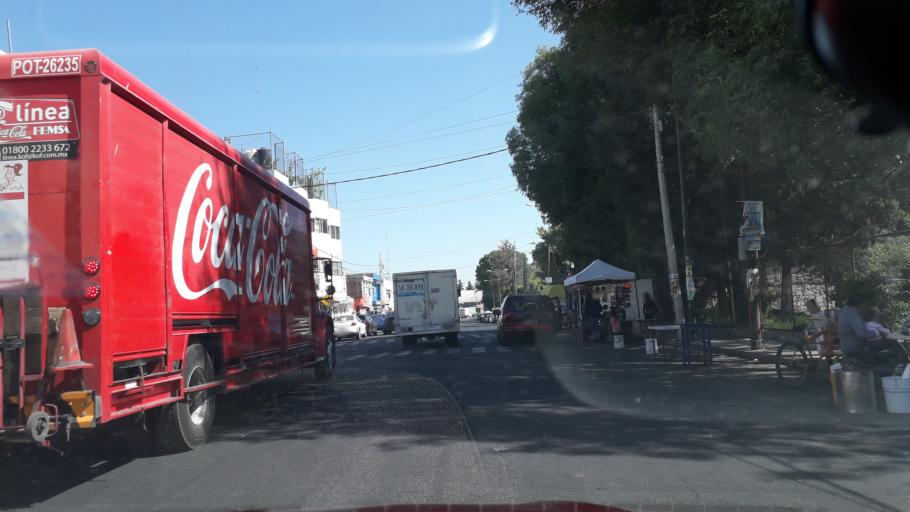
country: MX
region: Puebla
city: Puebla
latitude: 19.0769
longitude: -98.2114
